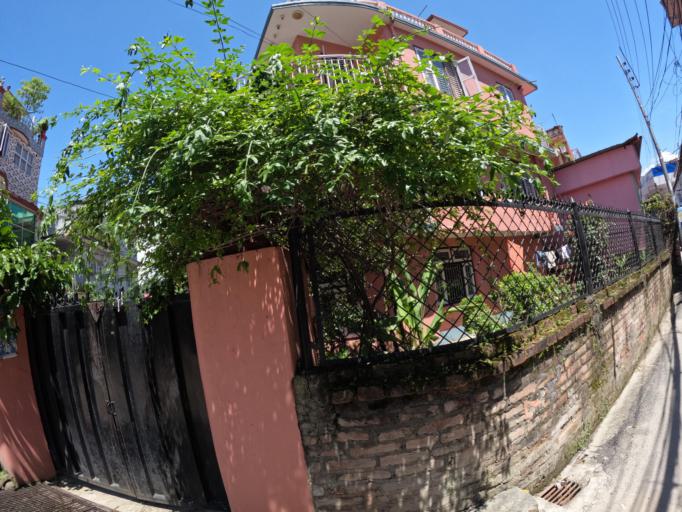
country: NP
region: Central Region
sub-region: Bagmati Zone
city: Kathmandu
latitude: 27.7431
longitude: 85.3256
